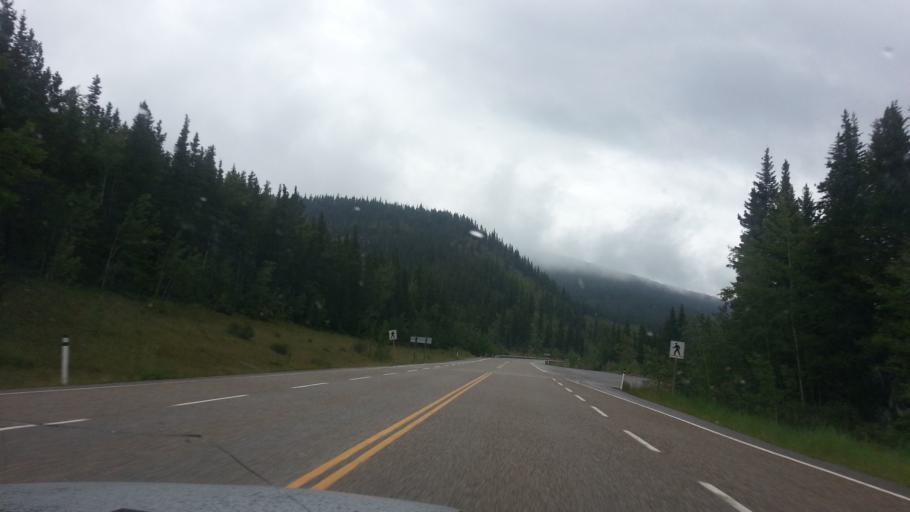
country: CA
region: Alberta
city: Cochrane
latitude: 50.8649
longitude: -114.7912
